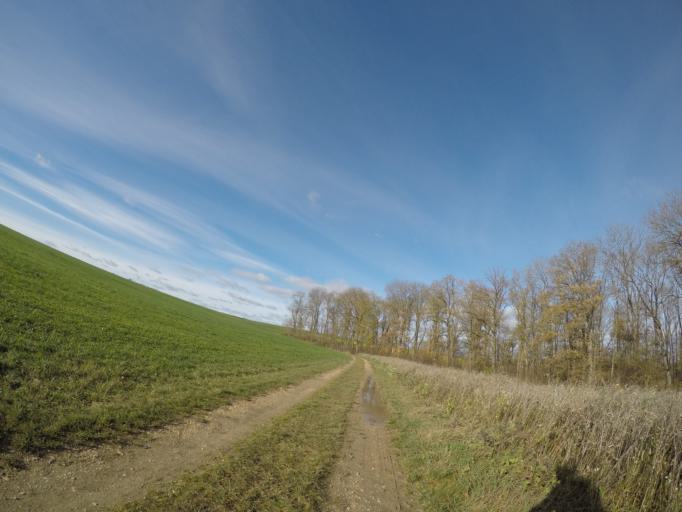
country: DE
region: Baden-Wuerttemberg
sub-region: Tuebingen Region
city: Dornstadt
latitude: 48.4447
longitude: 9.9344
